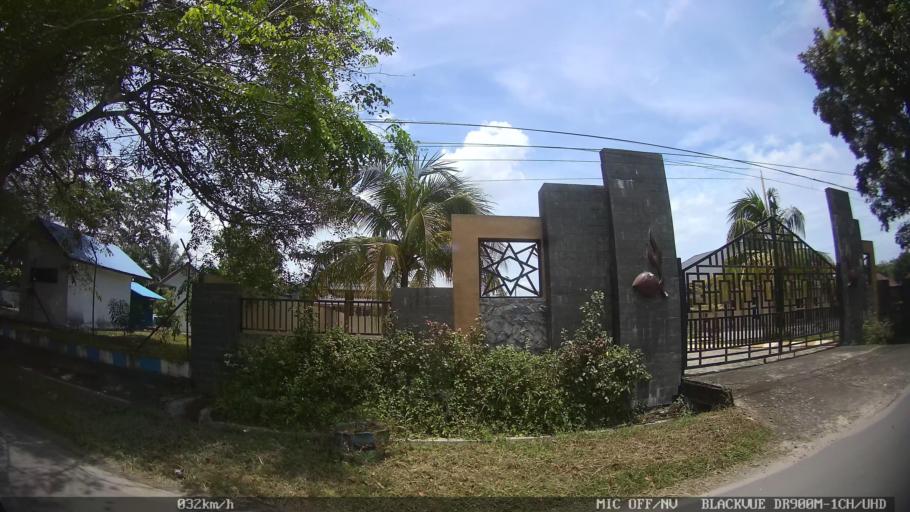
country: ID
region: North Sumatra
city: Percut
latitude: 3.5407
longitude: 98.8735
